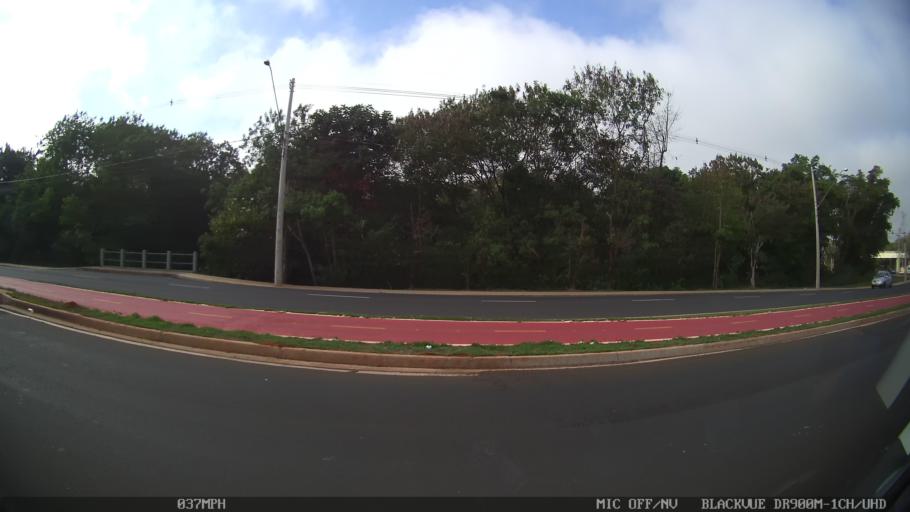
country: BR
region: Sao Paulo
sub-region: Sao Jose Do Rio Preto
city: Sao Jose do Rio Preto
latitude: -20.8133
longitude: -49.4343
